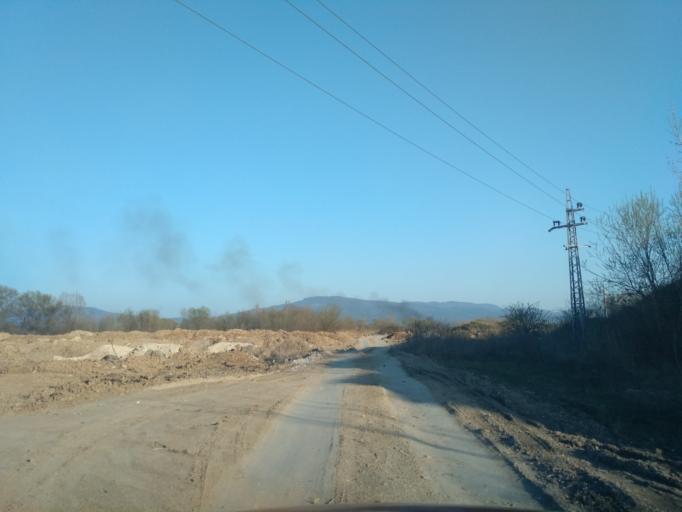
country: SK
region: Kosicky
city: Kosice
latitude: 48.6695
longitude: 21.3013
